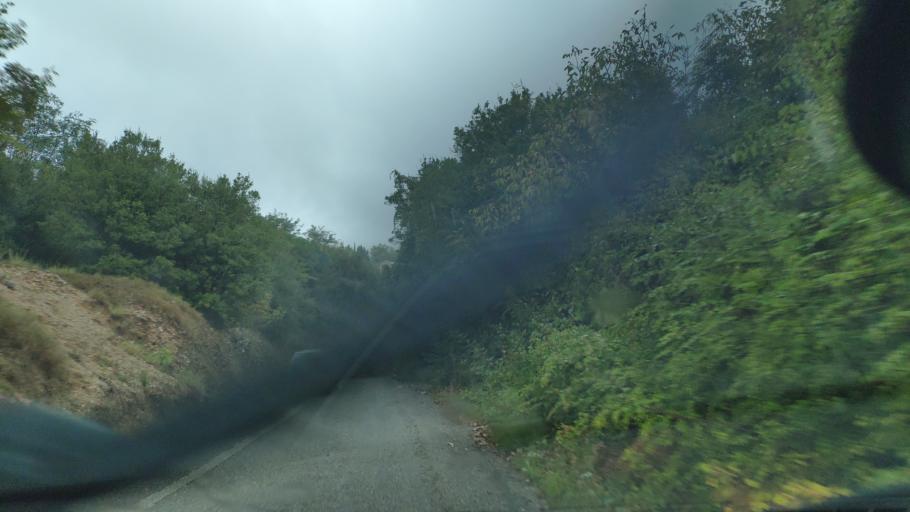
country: GR
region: West Greece
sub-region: Nomos Aitolias kai Akarnanias
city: Krikellos
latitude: 39.0270
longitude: 21.3221
